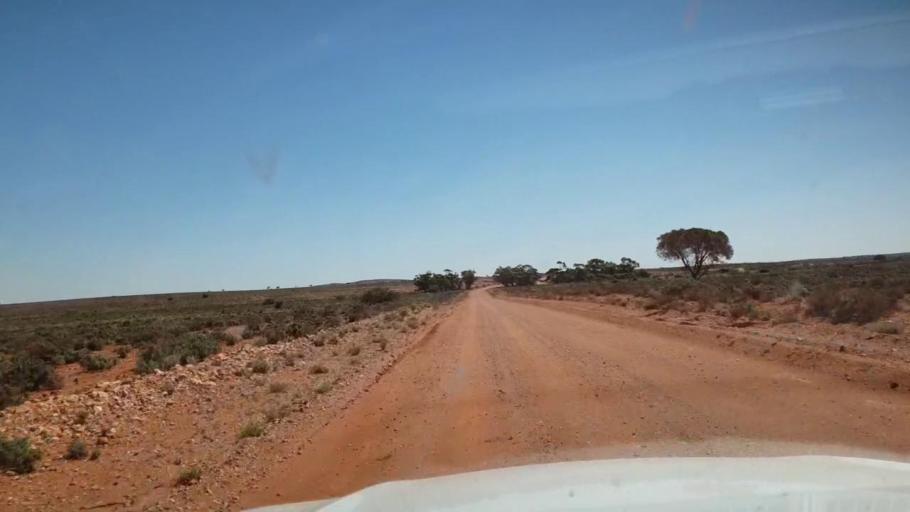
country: AU
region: South Australia
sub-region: Whyalla
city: Whyalla
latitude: -32.6830
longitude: 137.0927
